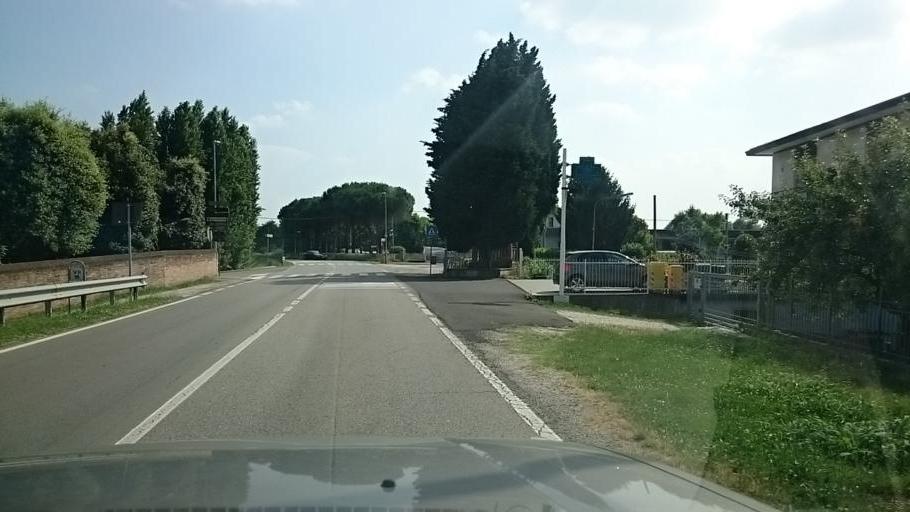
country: IT
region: Veneto
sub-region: Provincia di Padova
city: Tavo
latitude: 45.5007
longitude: 11.8547
